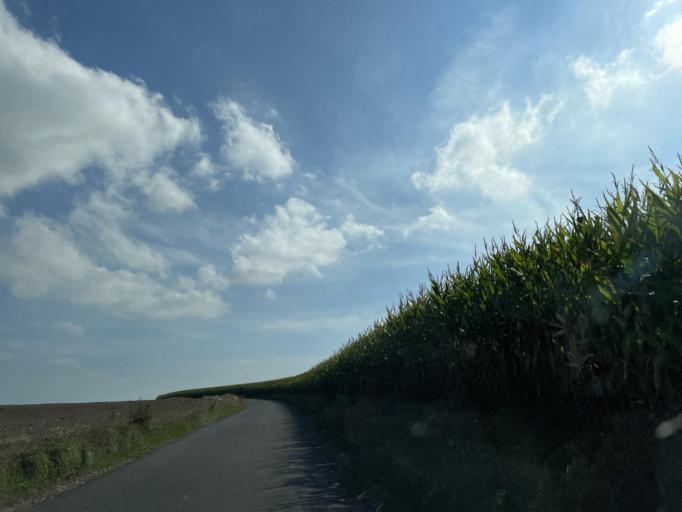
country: FR
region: Haute-Normandie
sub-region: Departement de la Seine-Maritime
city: Criel-sur-Mer
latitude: 50.0360
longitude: 1.3425
